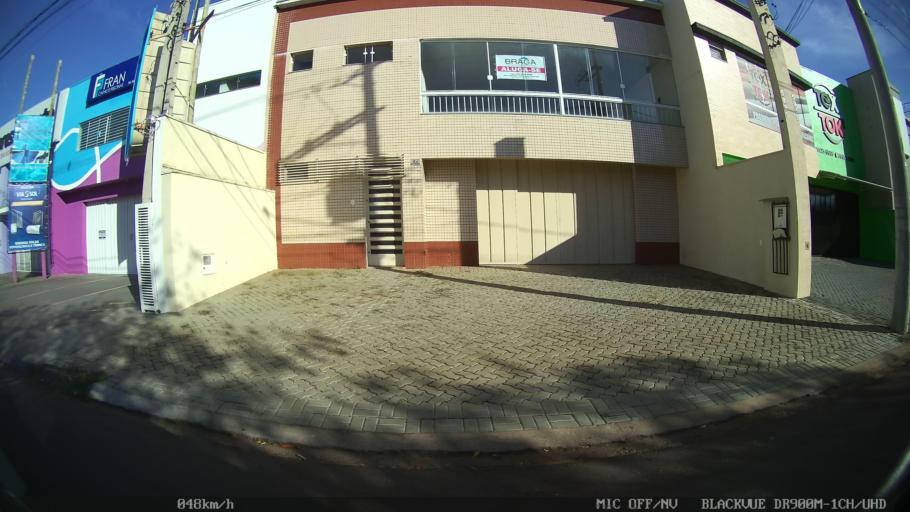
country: BR
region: Sao Paulo
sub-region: Franca
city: Franca
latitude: -20.5070
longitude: -47.3977
